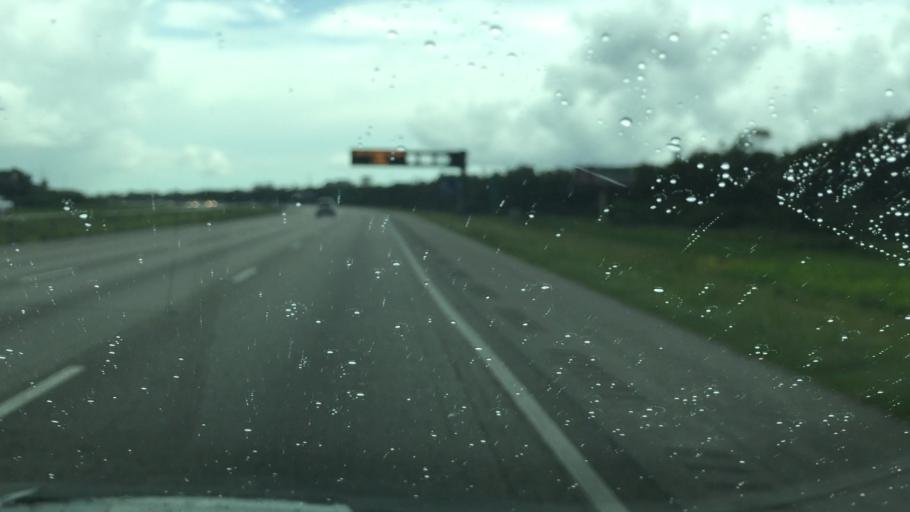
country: US
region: Florida
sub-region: Lee County
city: Fort Myers
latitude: 26.6283
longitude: -81.8075
